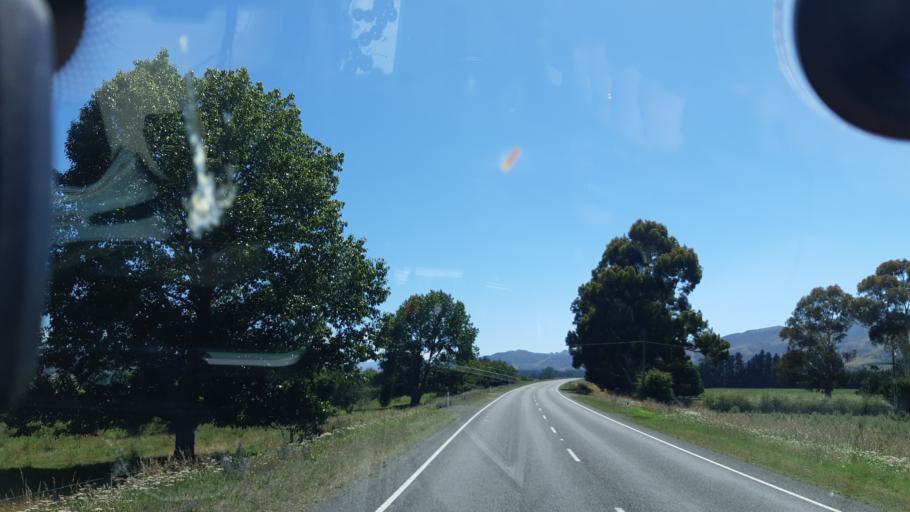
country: NZ
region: Canterbury
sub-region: Kaikoura District
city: Kaikoura
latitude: -42.7089
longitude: 173.2940
